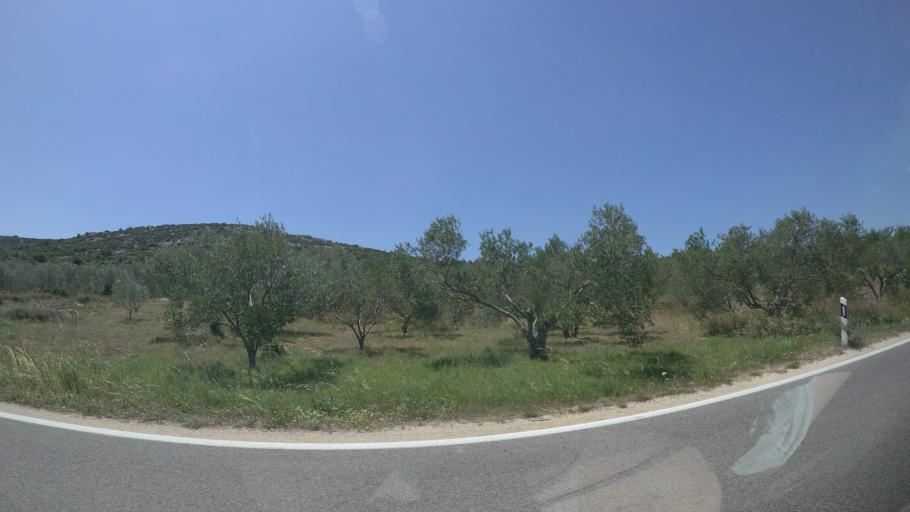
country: HR
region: Sibensko-Kniniska
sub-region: Grad Sibenik
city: Pirovac
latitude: 43.8024
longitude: 15.6736
